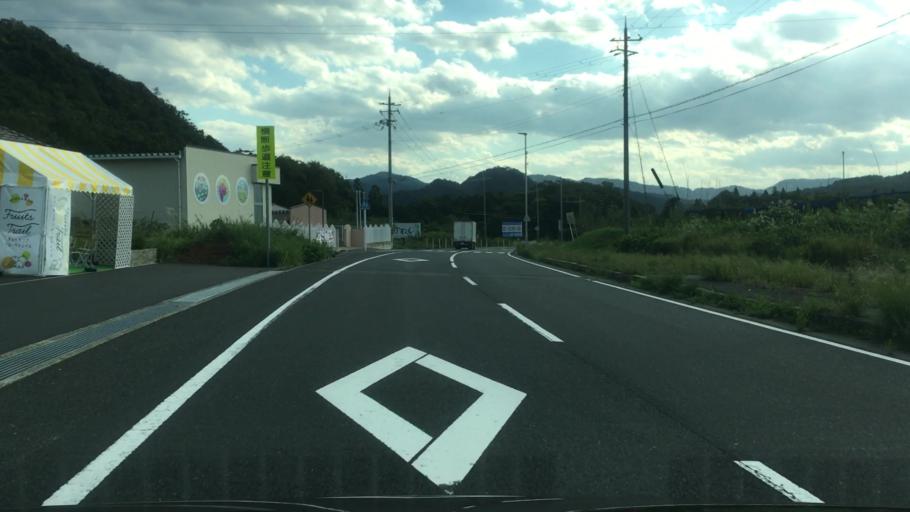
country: JP
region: Hyogo
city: Toyooka
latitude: 35.6221
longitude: 134.9282
